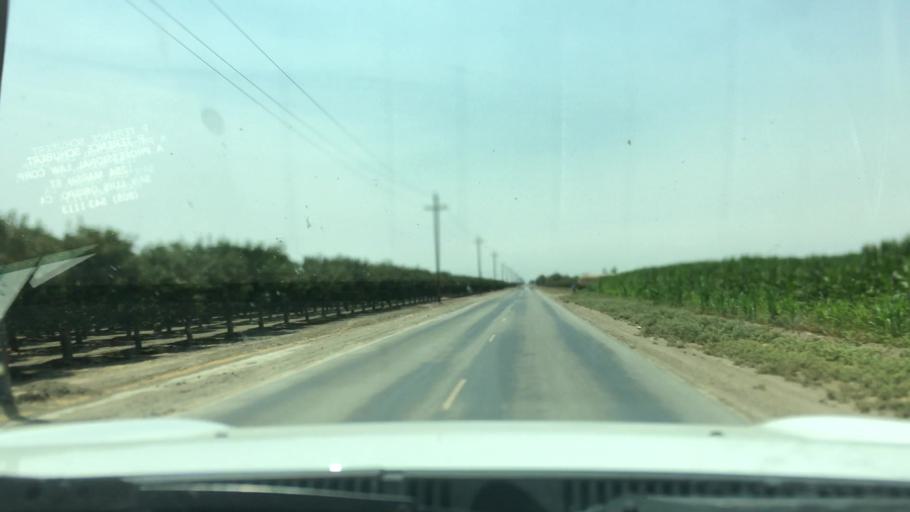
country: US
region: California
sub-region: Kern County
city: Wasco
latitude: 35.6935
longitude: -119.4374
